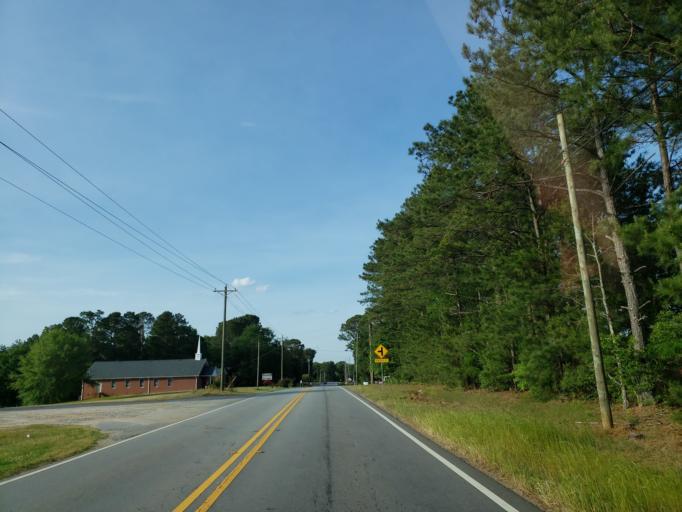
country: US
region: Georgia
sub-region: Carroll County
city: Bowdon
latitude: 33.5200
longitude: -85.2595
